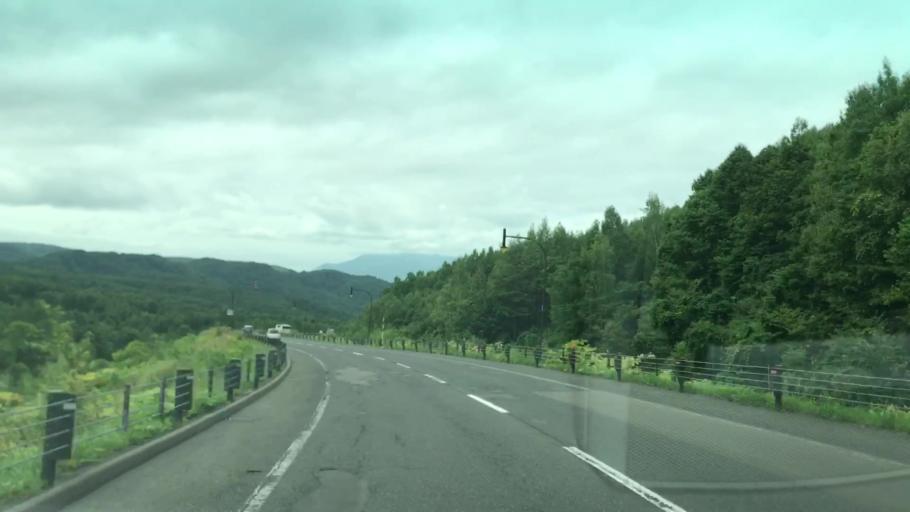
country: JP
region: Hokkaido
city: Niseko Town
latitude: 42.9550
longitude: 140.8645
